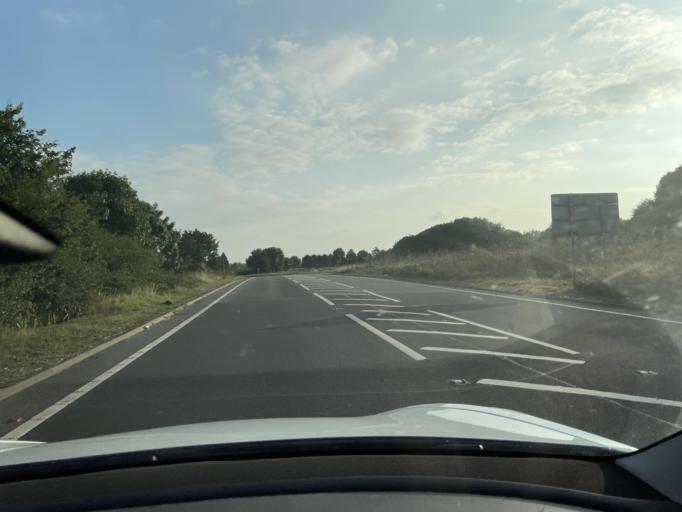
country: GB
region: England
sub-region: Bedford
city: Pertenhall
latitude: 52.3604
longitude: -0.4038
